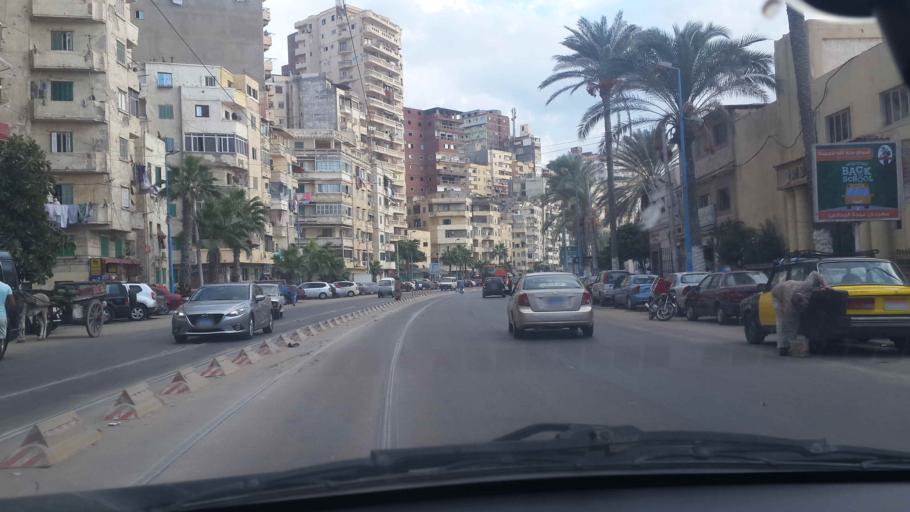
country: EG
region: Alexandria
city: Alexandria
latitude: 31.2092
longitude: 29.8792
